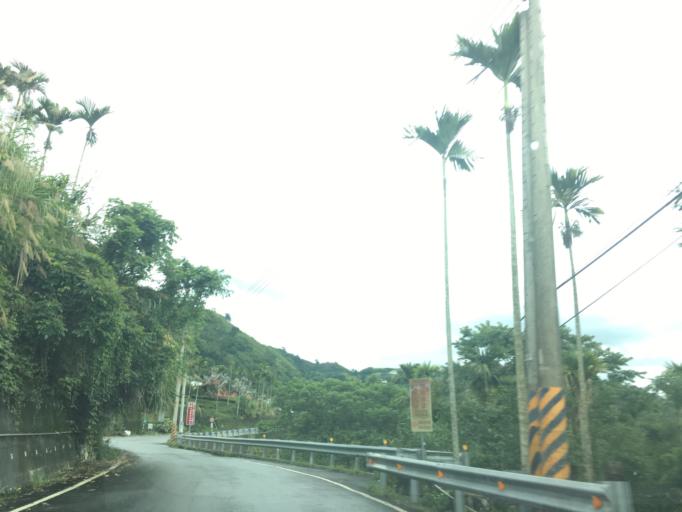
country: TW
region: Taiwan
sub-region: Yunlin
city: Douliu
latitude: 23.5576
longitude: 120.6637
